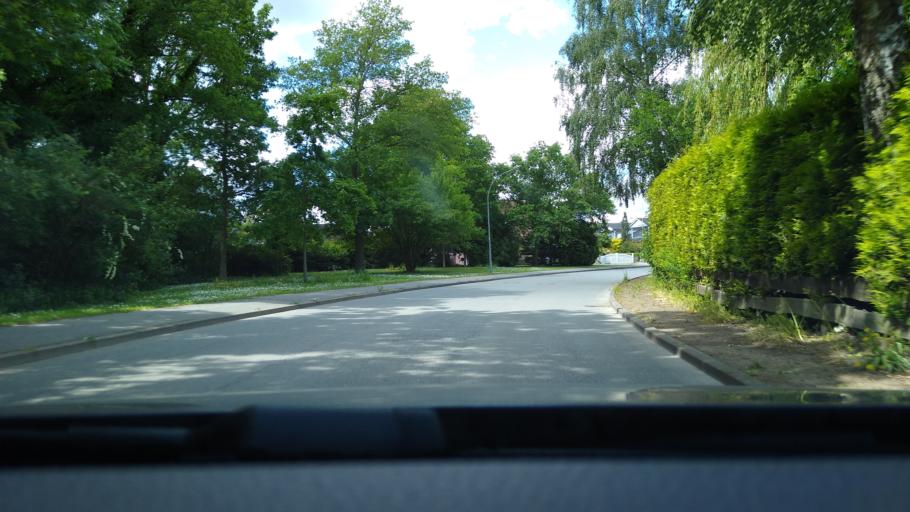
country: DE
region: Schleswig-Holstein
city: Kabelhorst
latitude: 54.2295
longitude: 10.9236
